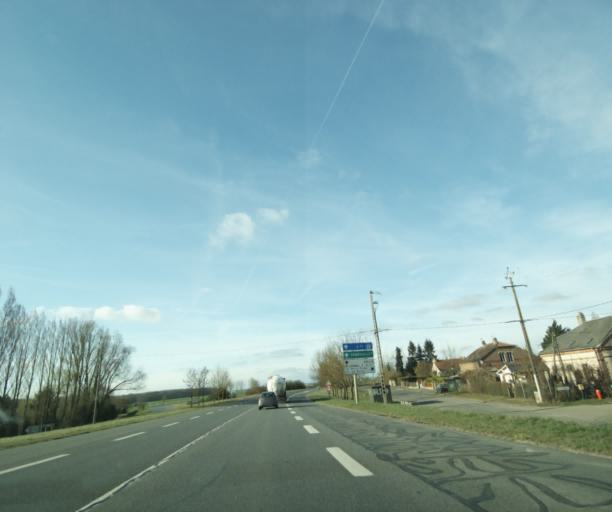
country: FR
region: Ile-de-France
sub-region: Departement des Yvelines
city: Ablis
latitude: 48.4789
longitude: 1.8503
